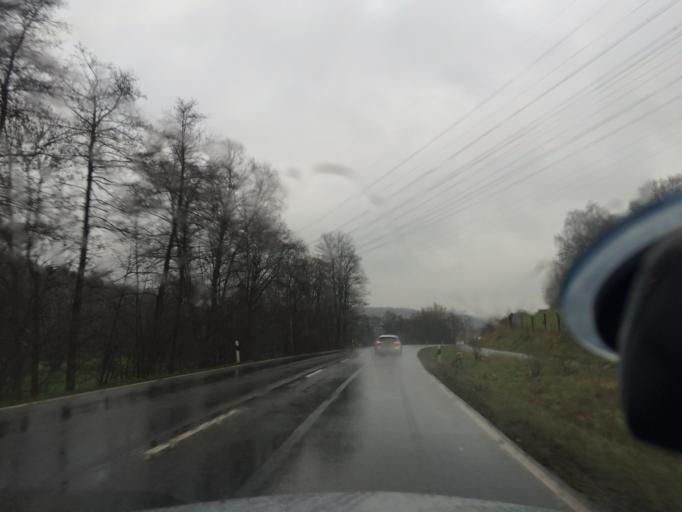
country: DE
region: Hesse
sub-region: Regierungsbezirk Giessen
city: Fronhausen
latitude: 50.7112
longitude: 8.7491
